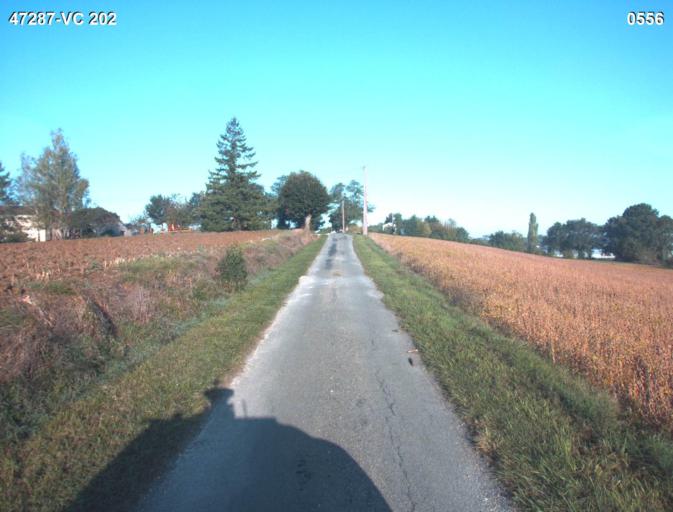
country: FR
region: Aquitaine
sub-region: Departement du Lot-et-Garonne
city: Laplume
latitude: 44.1150
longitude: 0.4646
